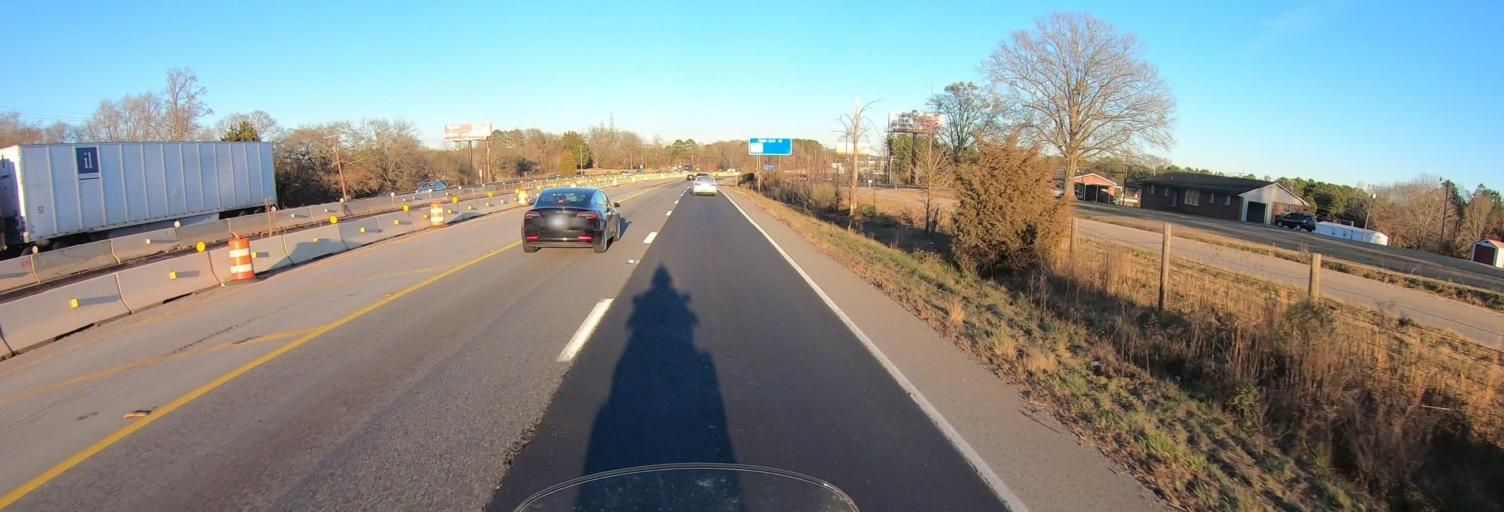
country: US
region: South Carolina
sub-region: Cherokee County
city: East Gaffney
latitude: 35.0991
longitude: -81.6430
